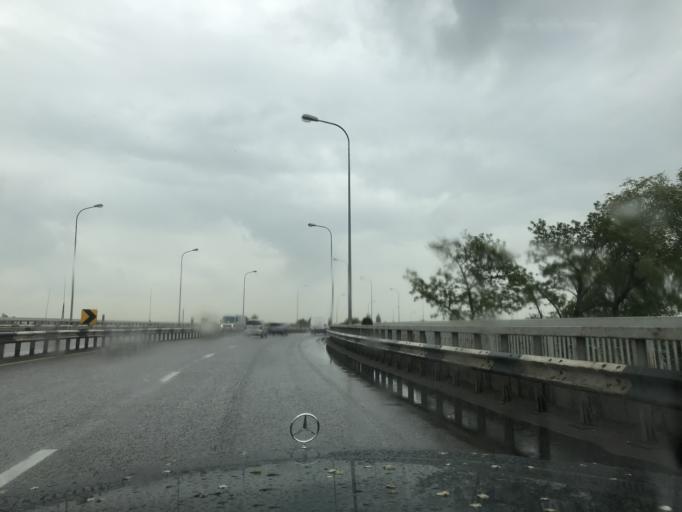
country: KZ
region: Almaty Oblysy
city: Pervomayskiy
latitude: 43.3365
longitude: 76.9636
